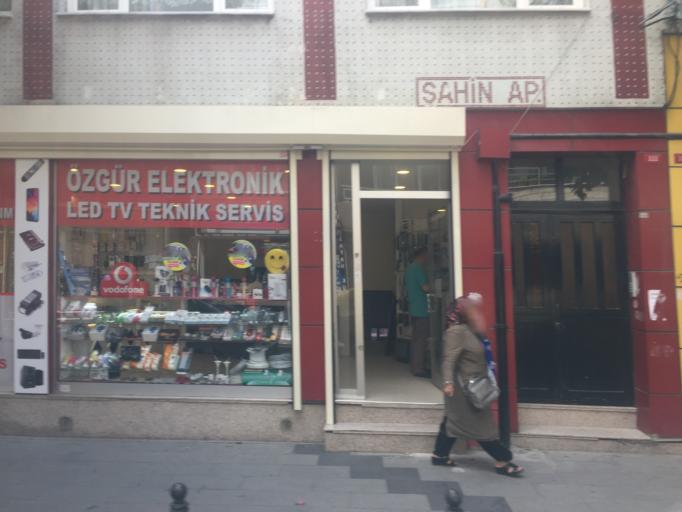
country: TR
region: Istanbul
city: Esenler
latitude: 41.0503
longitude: 28.9067
